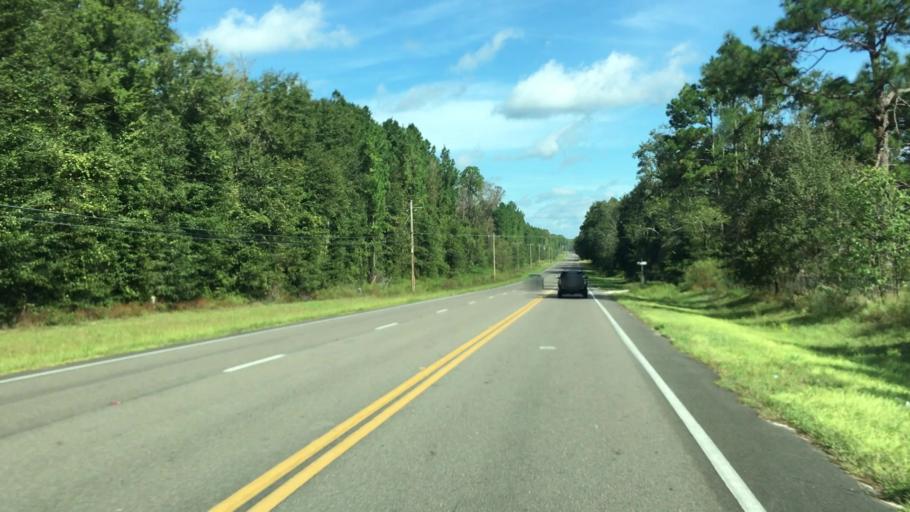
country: US
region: Florida
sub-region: Alachua County
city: Gainesville
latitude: 29.7277
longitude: -82.2769
